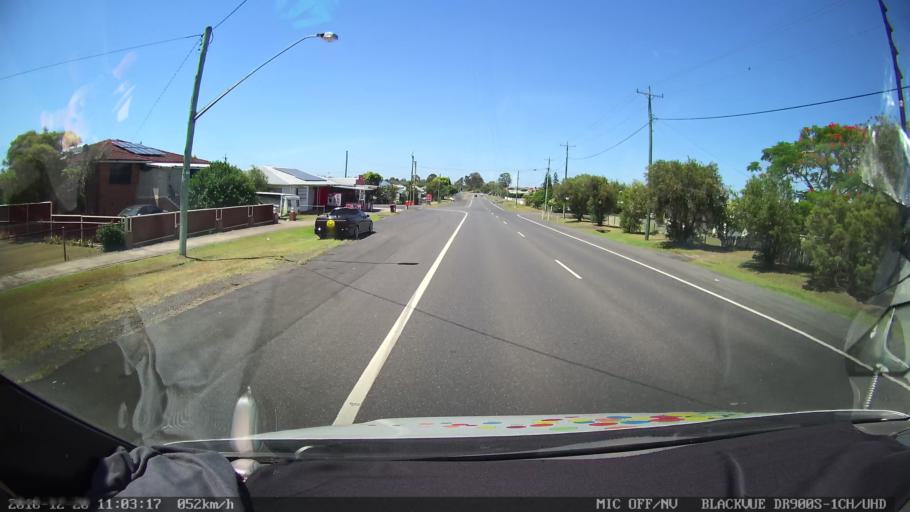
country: AU
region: New South Wales
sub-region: Richmond Valley
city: Casino
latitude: -28.8757
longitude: 153.0433
